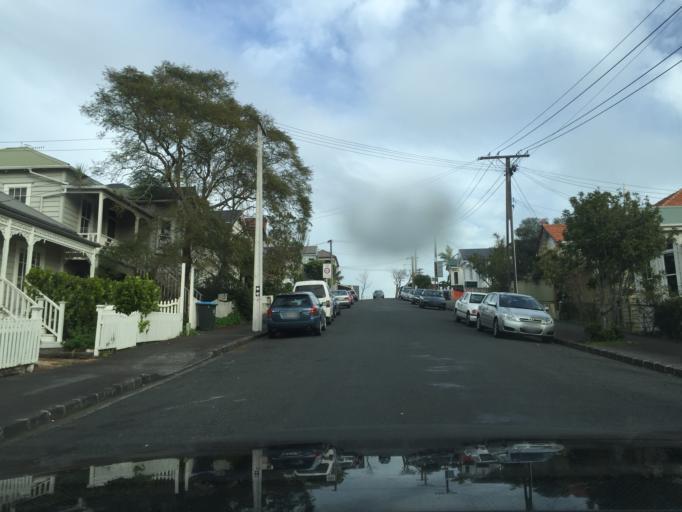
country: NZ
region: Auckland
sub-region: Auckland
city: Auckland
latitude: -36.8547
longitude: 174.7404
